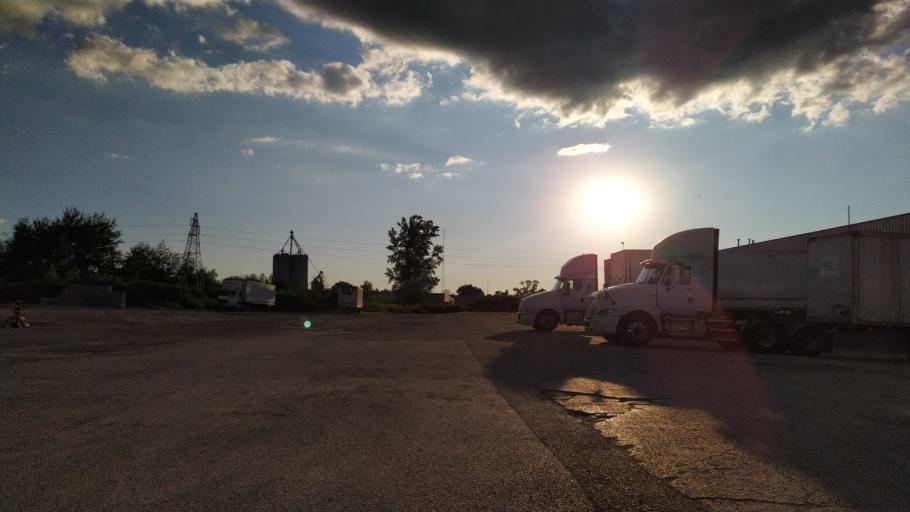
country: CA
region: Ontario
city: Stratford
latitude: 43.3647
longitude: -80.9536
